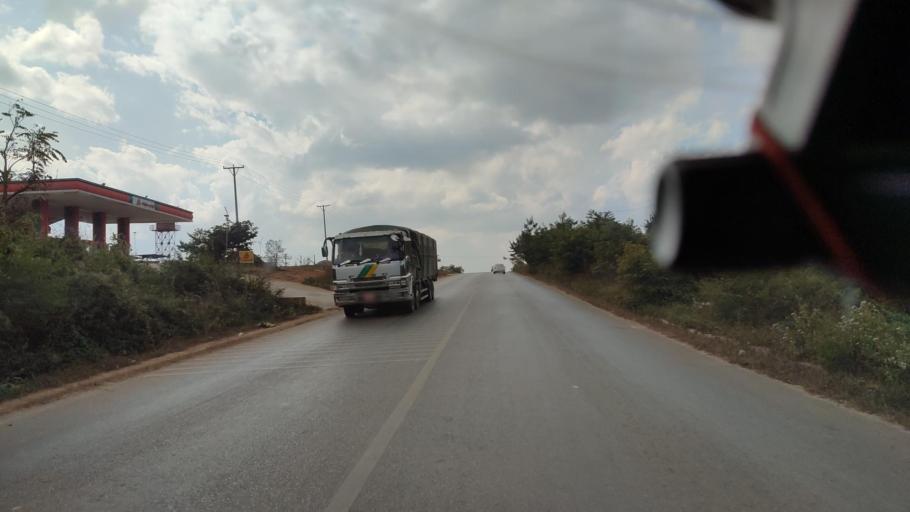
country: MM
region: Shan
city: Lashio
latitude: 22.9472
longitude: 97.6955
